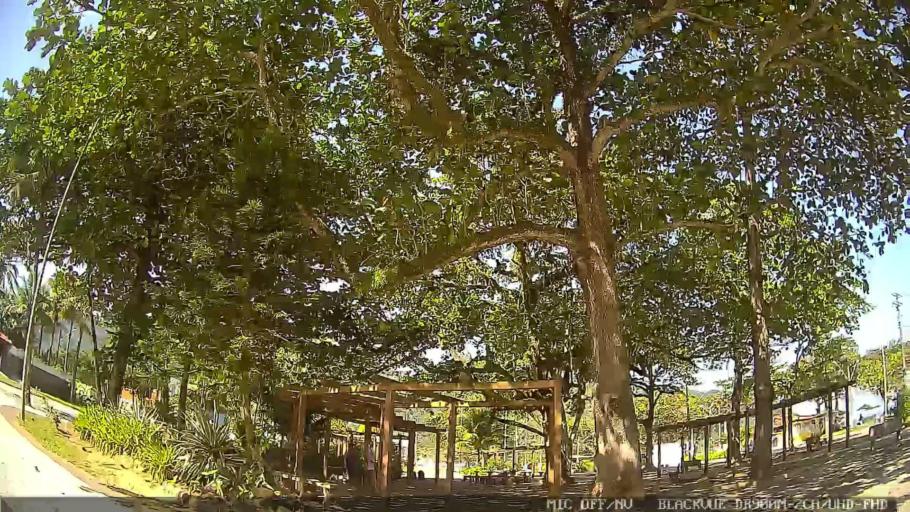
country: BR
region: Sao Paulo
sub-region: Guaruja
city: Guaruja
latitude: -24.0184
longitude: -46.2950
